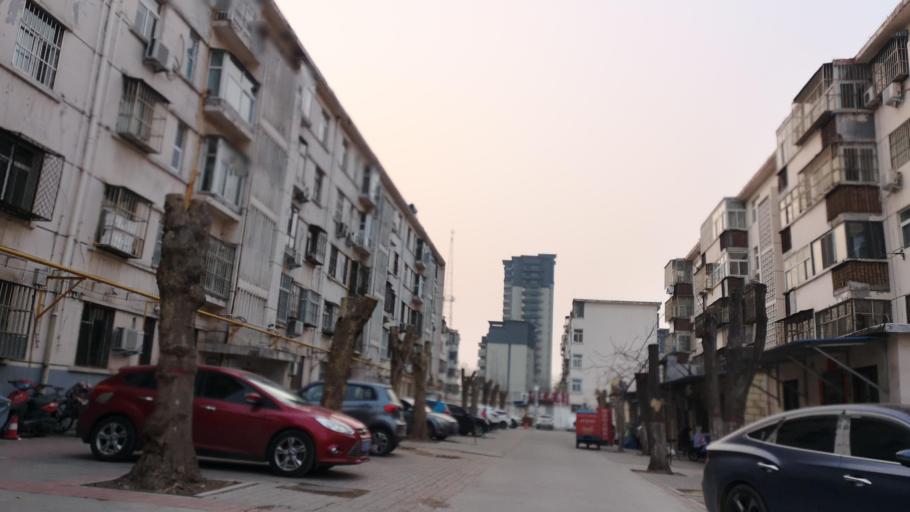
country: CN
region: Henan Sheng
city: Zhongyuanlu
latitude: 35.7814
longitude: 115.0756
